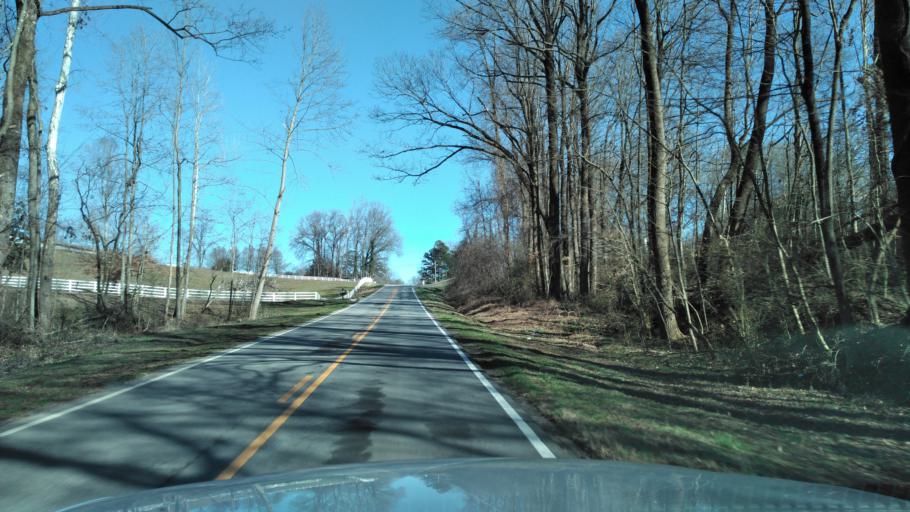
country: US
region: Georgia
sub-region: Hall County
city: Gainesville
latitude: 34.3103
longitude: -83.7303
